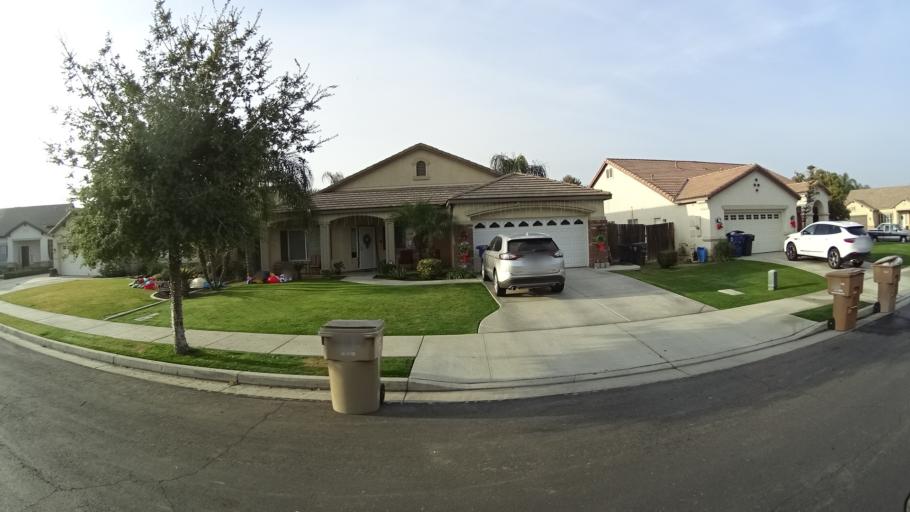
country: US
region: California
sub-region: Kern County
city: Greenacres
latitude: 35.4258
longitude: -119.1232
